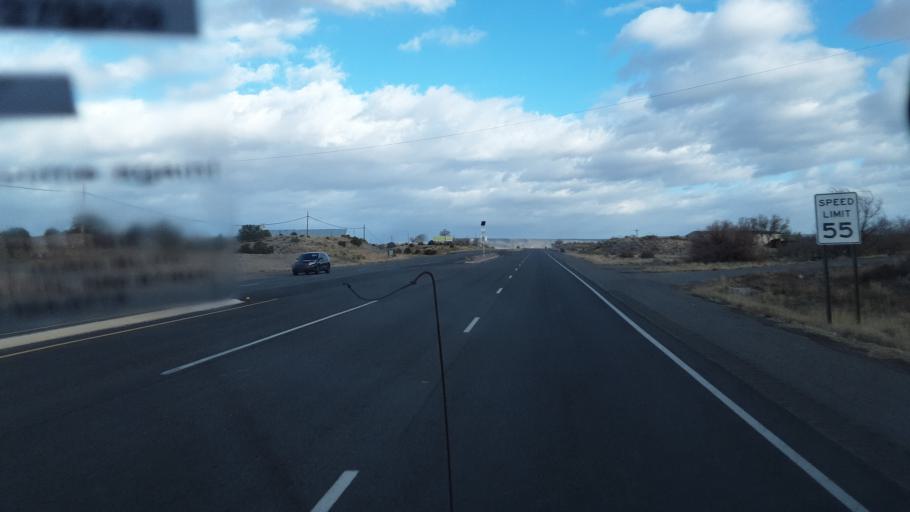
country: US
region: New Mexico
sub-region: Rio Arriba County
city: Espanola
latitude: 36.0138
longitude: -106.0891
